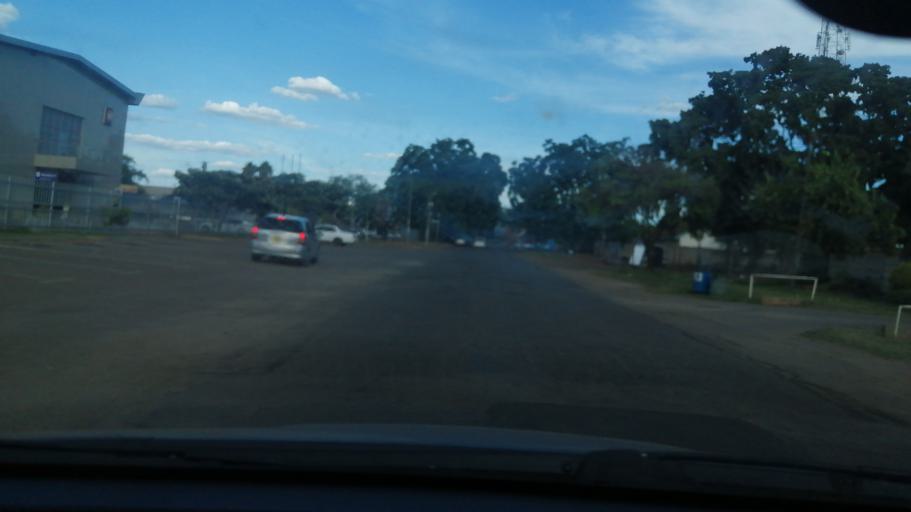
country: ZW
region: Harare
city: Harare
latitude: -17.7612
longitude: 31.0848
